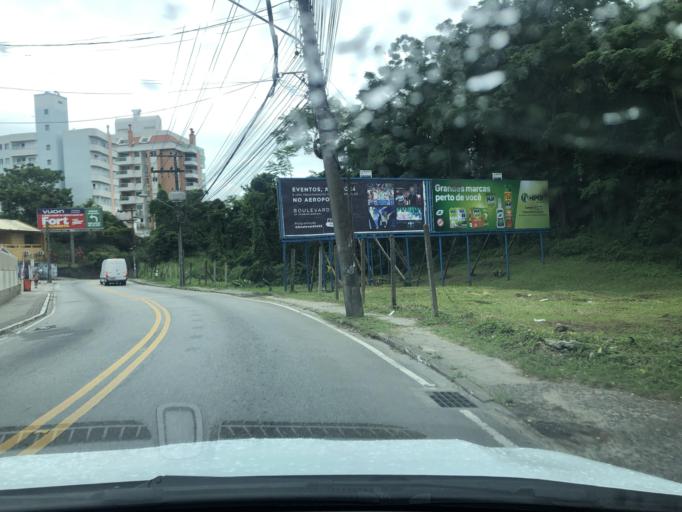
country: BR
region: Santa Catarina
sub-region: Florianopolis
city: Pantanal
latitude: -27.6113
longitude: -48.5250
